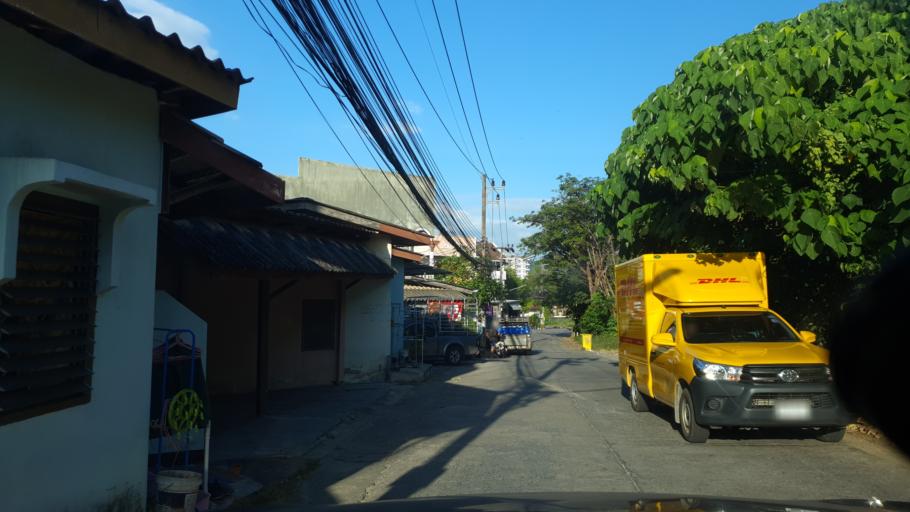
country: TH
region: Phuket
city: Kathu
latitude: 7.9028
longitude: 98.3325
